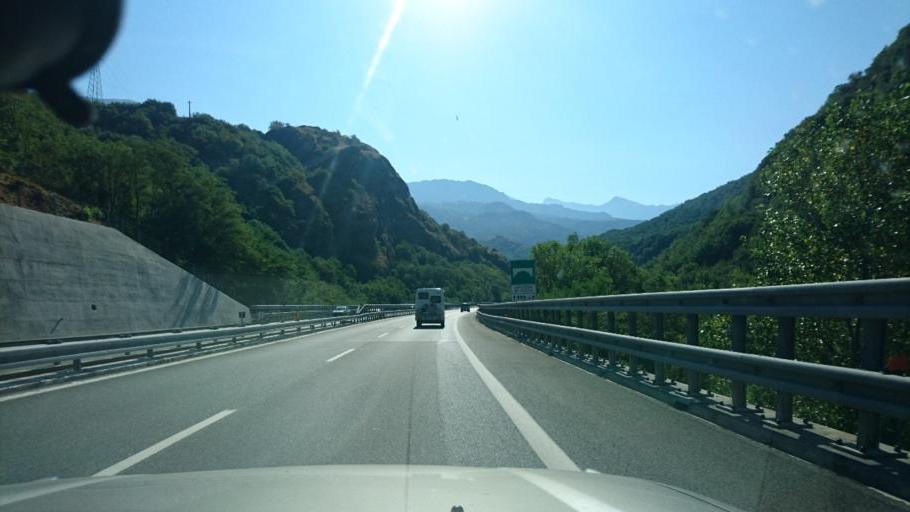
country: IT
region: Aosta Valley
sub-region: Valle d'Aosta
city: Saint-Vincent
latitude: 45.7395
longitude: 7.6502
